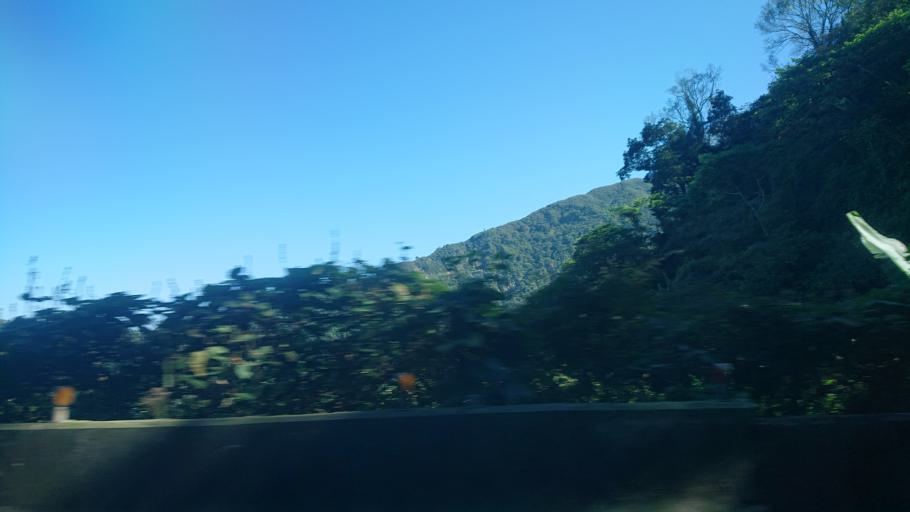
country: TW
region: Taiwan
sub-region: Chiayi
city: Jiayi Shi
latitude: 23.5170
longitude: 120.6216
